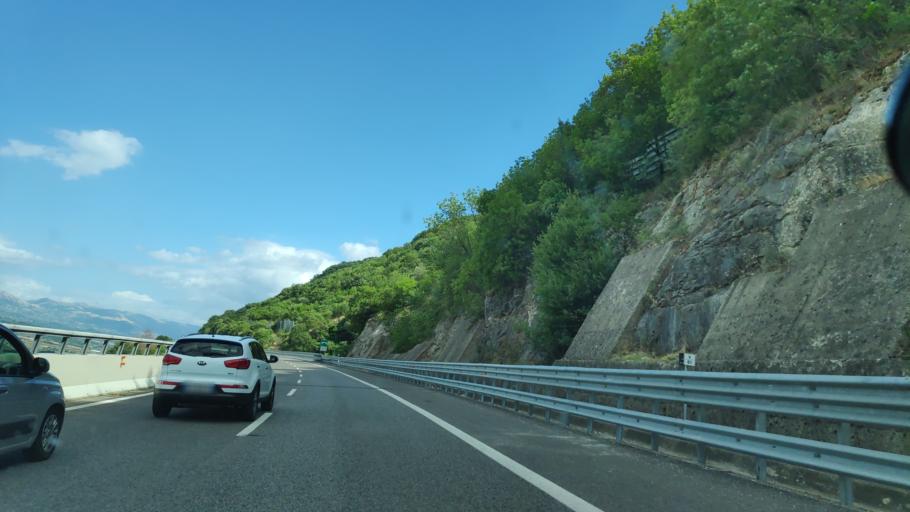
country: IT
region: Campania
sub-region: Provincia di Salerno
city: Sicignano degli Alburni
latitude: 40.5929
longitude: 15.3247
